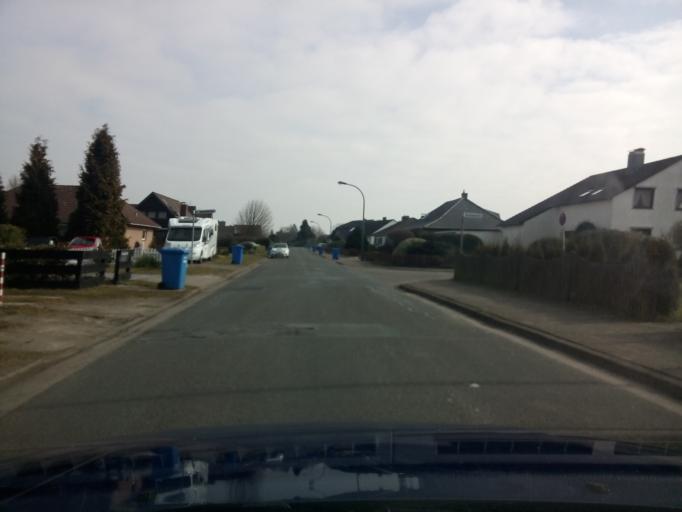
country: DE
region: Lower Saxony
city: Ritterhude
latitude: 53.2073
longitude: 8.7619
